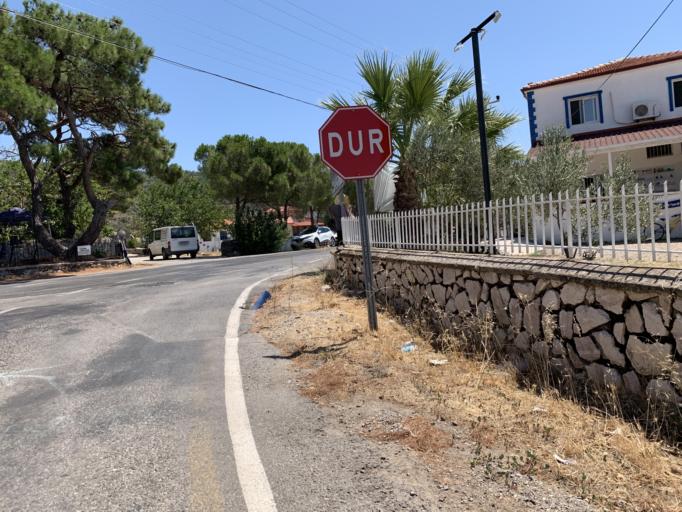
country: TR
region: Izmir
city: Uzunkuyu
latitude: 38.3220
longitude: 26.5780
